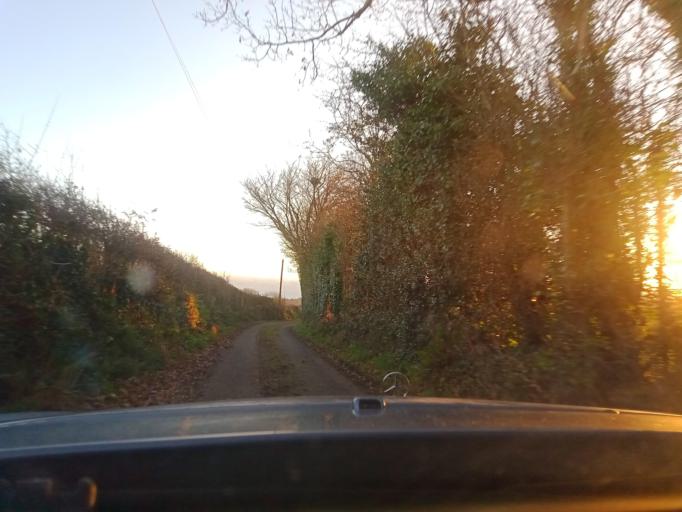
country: IE
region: Leinster
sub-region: Kilkenny
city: Graiguenamanagh
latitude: 52.4786
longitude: -6.9329
